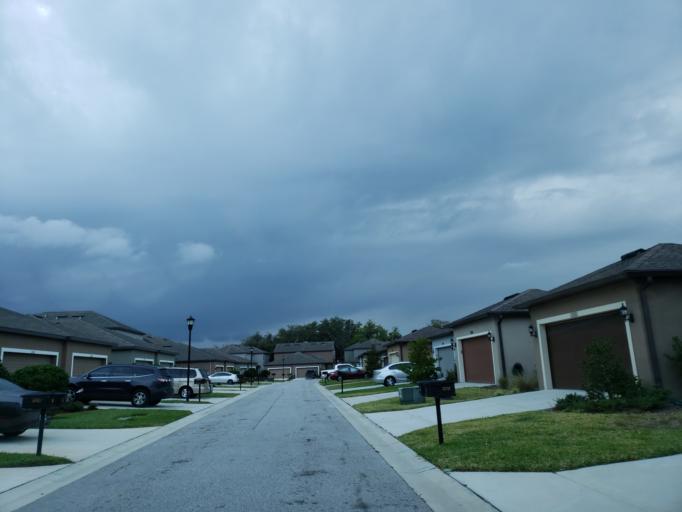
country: US
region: Florida
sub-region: Hillsborough County
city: Fish Hawk
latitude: 27.8516
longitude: -82.2535
